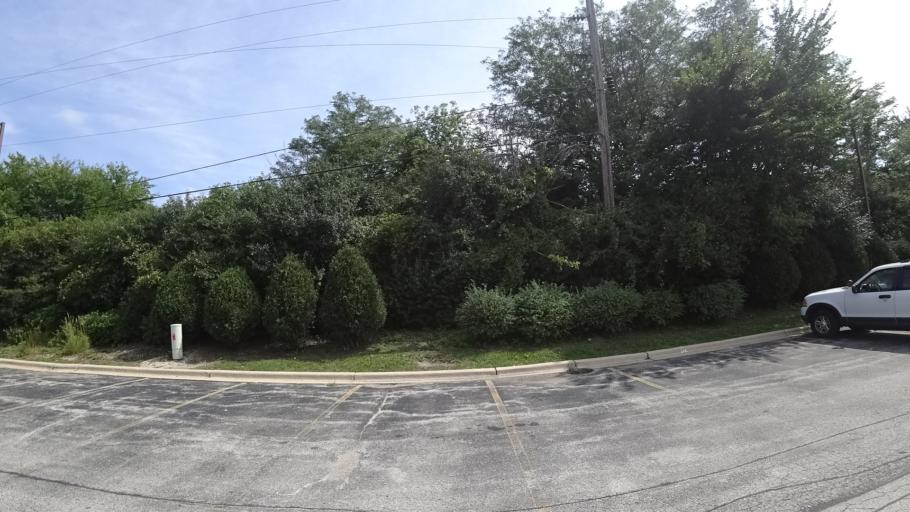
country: US
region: Illinois
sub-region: Cook County
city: Orland Hills
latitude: 41.5568
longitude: -87.8511
